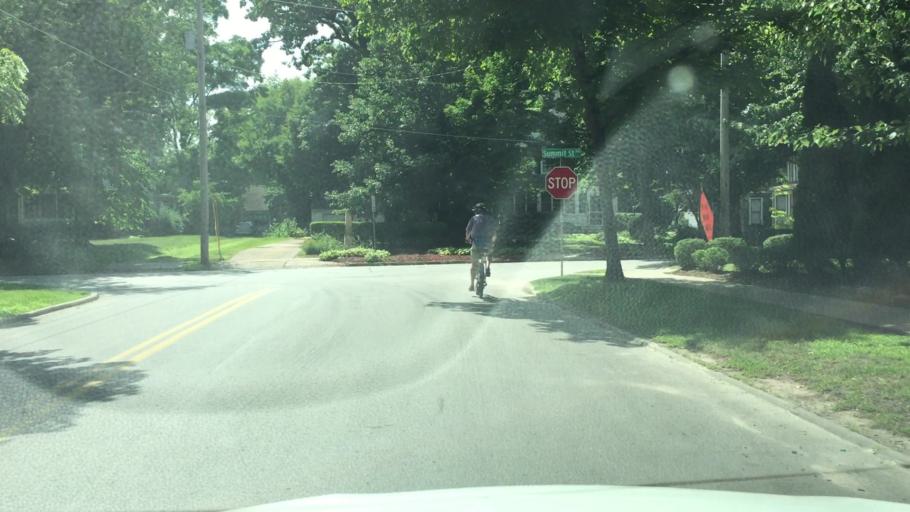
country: US
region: Iowa
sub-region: Johnson County
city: Iowa City
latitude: 41.6567
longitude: -91.5208
